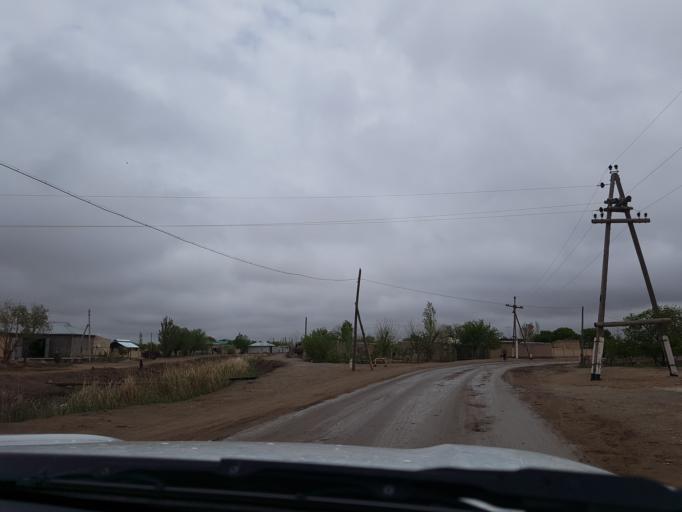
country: TM
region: Lebap
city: Sayat
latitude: 38.4574
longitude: 64.3753
